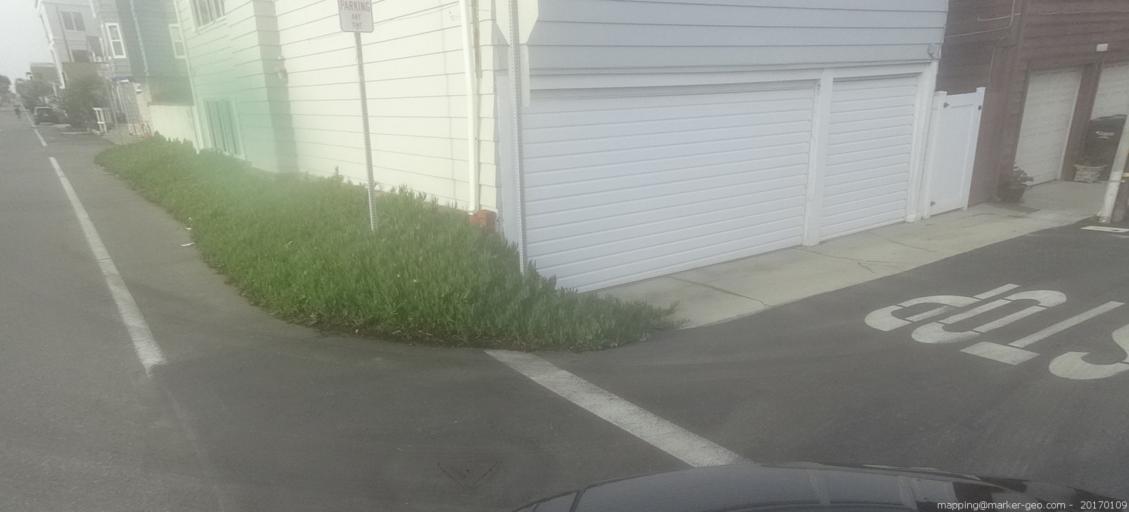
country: US
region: California
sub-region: Orange County
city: Seal Beach
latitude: 33.7140
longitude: -118.0668
